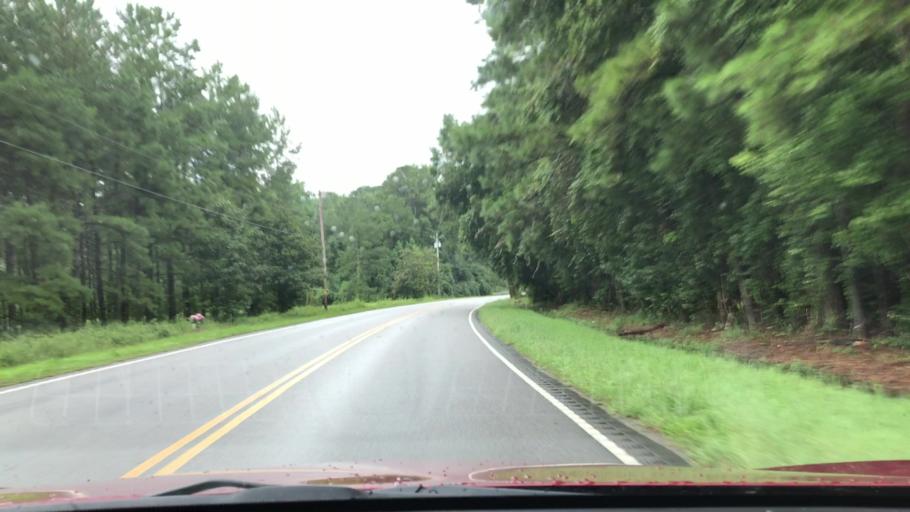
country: US
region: South Carolina
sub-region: Horry County
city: Conway
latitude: 33.7704
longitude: -79.0721
